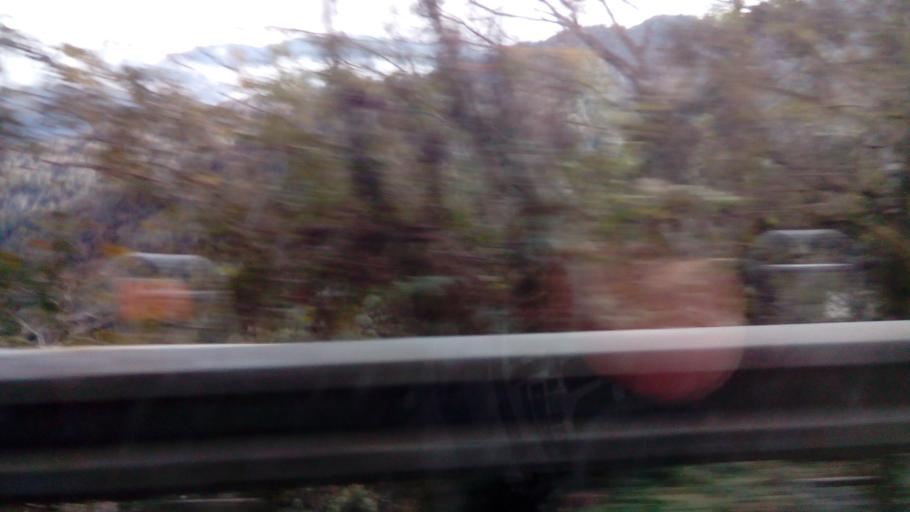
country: TW
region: Taiwan
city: Daxi
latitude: 24.4100
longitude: 121.3597
